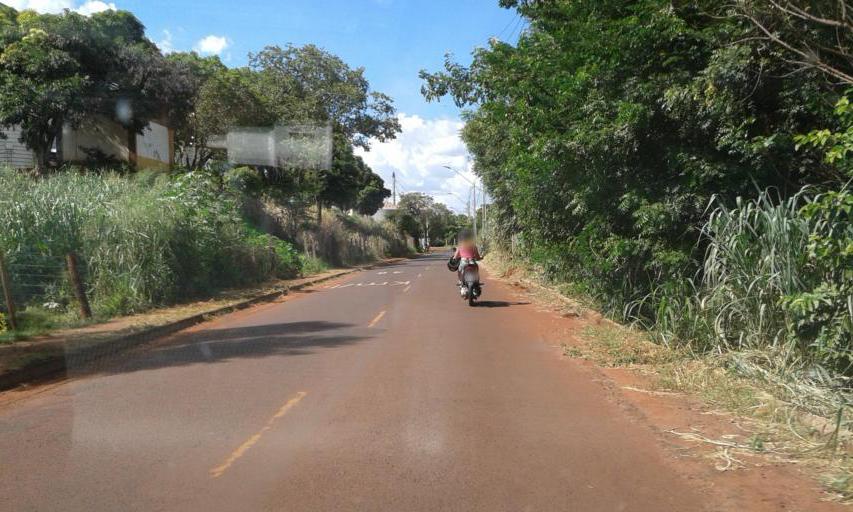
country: BR
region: Minas Gerais
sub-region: Ituiutaba
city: Ituiutaba
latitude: -18.9692
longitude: -49.4911
